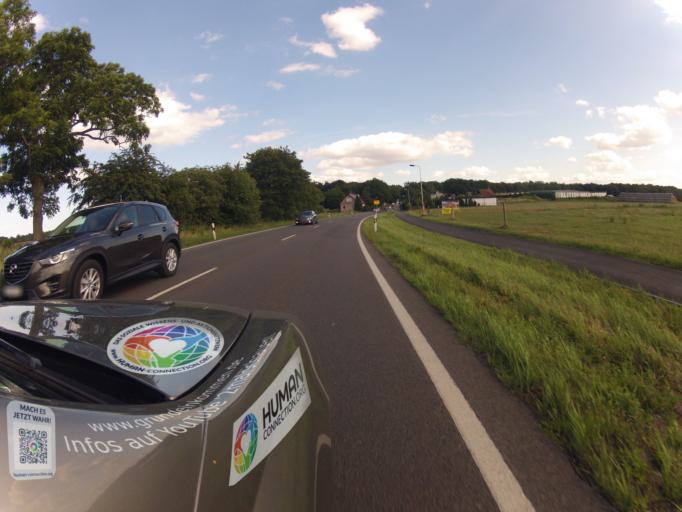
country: DE
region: Mecklenburg-Vorpommern
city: Loddin
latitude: 54.0311
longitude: 14.0292
